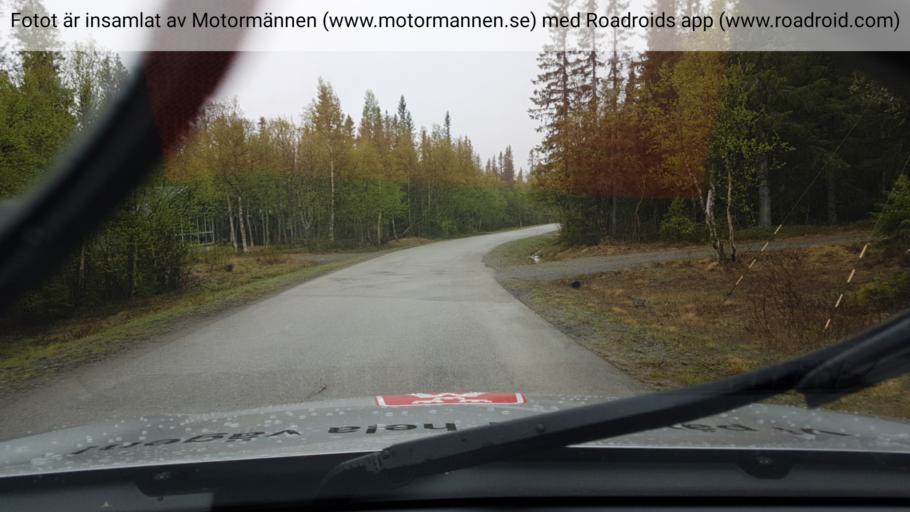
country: SE
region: Jaemtland
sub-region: Bergs Kommun
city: Hoverberg
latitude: 63.0249
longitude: 13.9452
